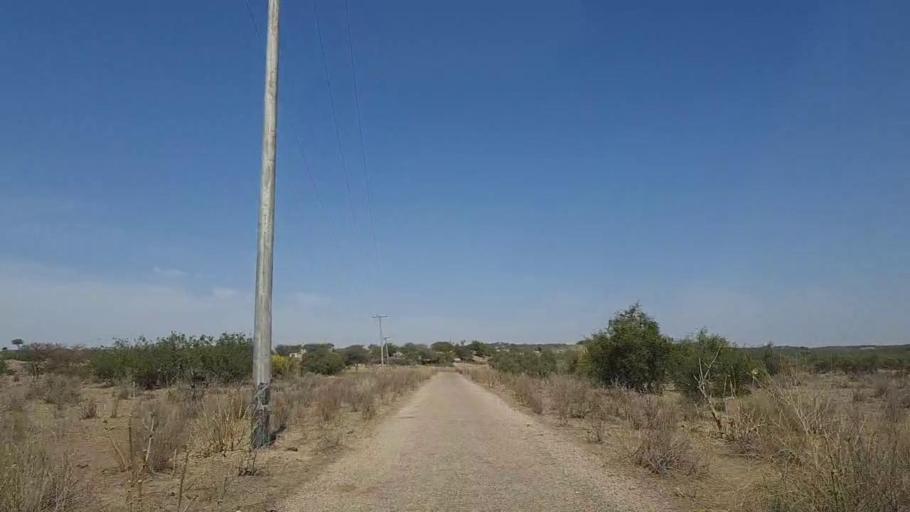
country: PK
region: Sindh
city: Mithi
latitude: 24.8486
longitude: 69.6706
